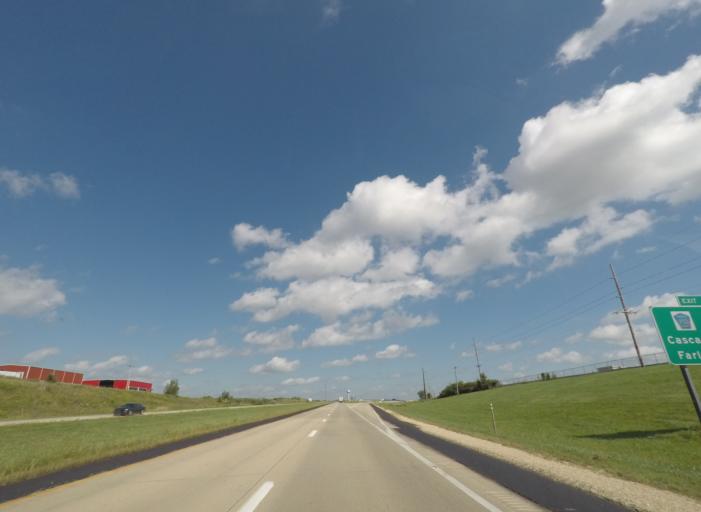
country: US
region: Iowa
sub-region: Dubuque County
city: Cascade
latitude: 42.3106
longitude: -91.0051
